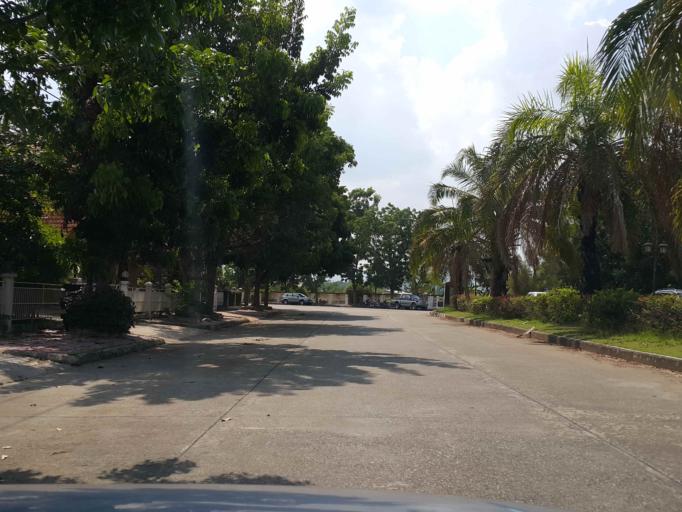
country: TH
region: Chiang Mai
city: Hang Dong
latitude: 18.7016
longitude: 98.9449
